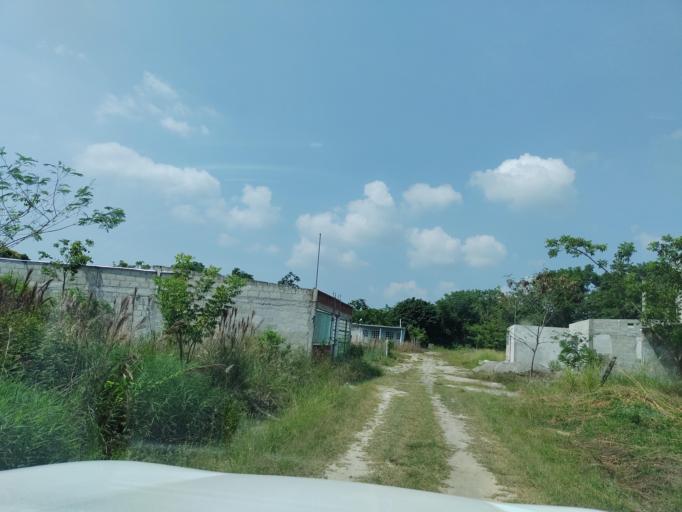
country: MX
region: Veracruz
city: Martinez de la Torre
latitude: 20.0881
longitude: -97.0549
